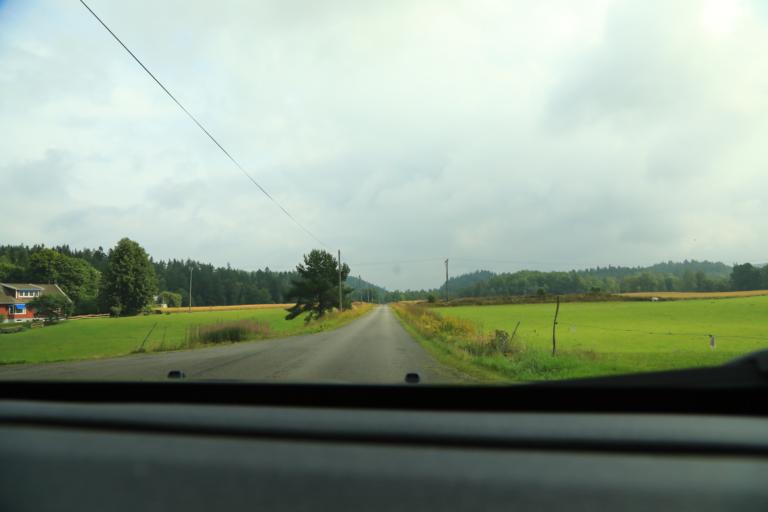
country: SE
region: Halland
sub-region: Falkenbergs Kommun
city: Falkenberg
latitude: 57.1152
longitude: 12.6864
